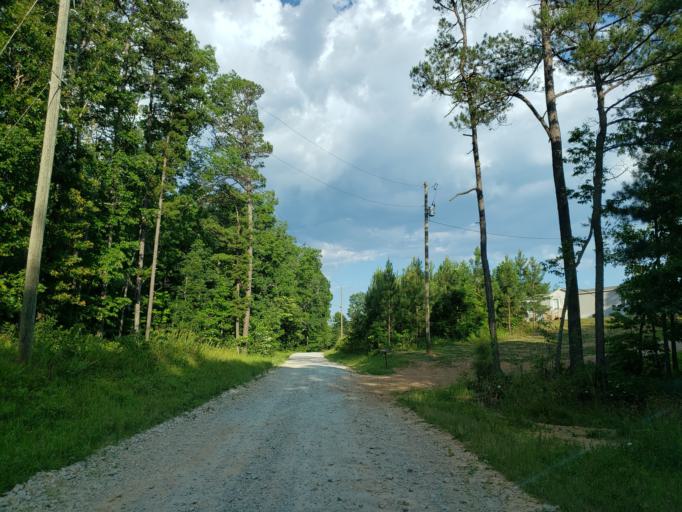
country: US
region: Georgia
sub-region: Haralson County
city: Buchanan
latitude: 33.8984
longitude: -85.3060
